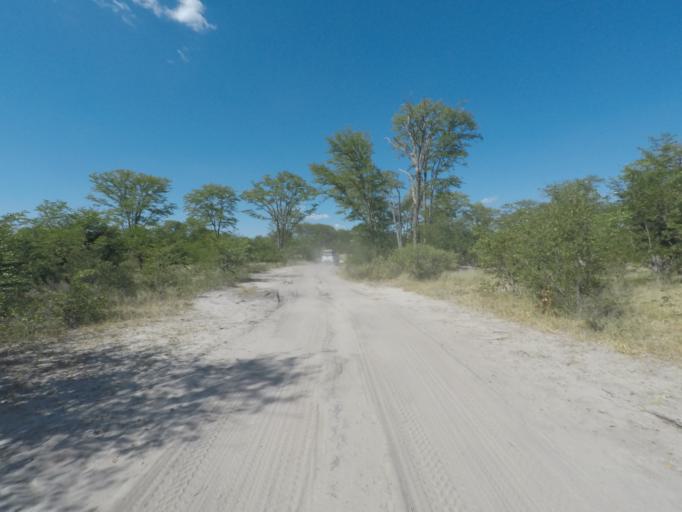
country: BW
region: North West
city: Maun
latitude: -19.4239
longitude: 23.6370
